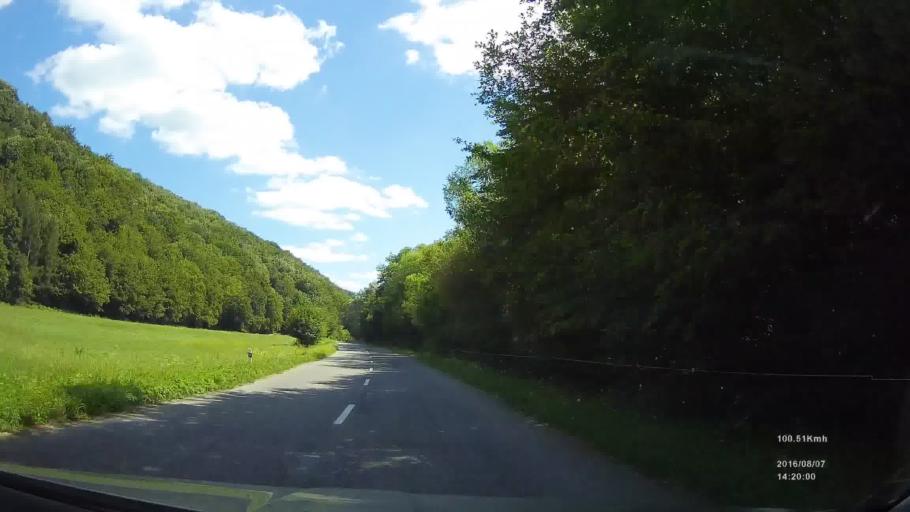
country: SK
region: Presovsky
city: Stropkov
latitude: 49.2959
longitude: 21.7577
